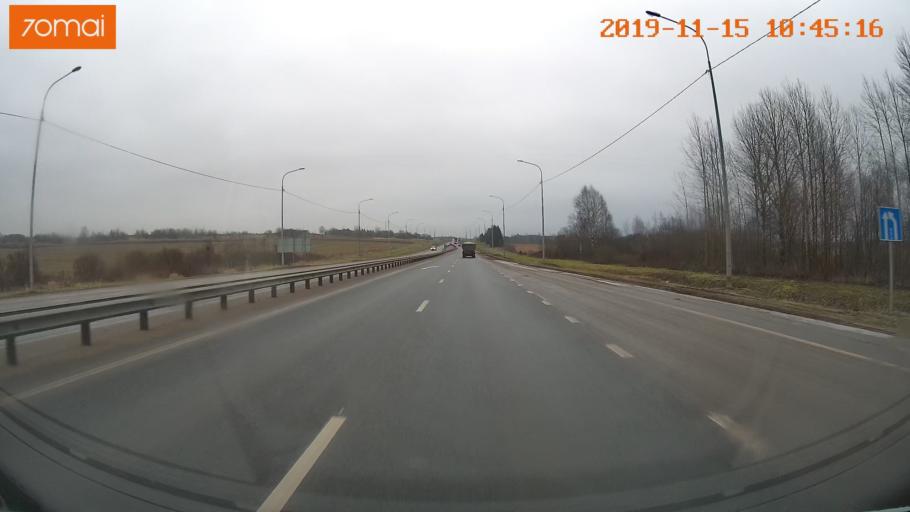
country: RU
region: Vologda
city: Sheksna
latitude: 59.2111
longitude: 38.5823
